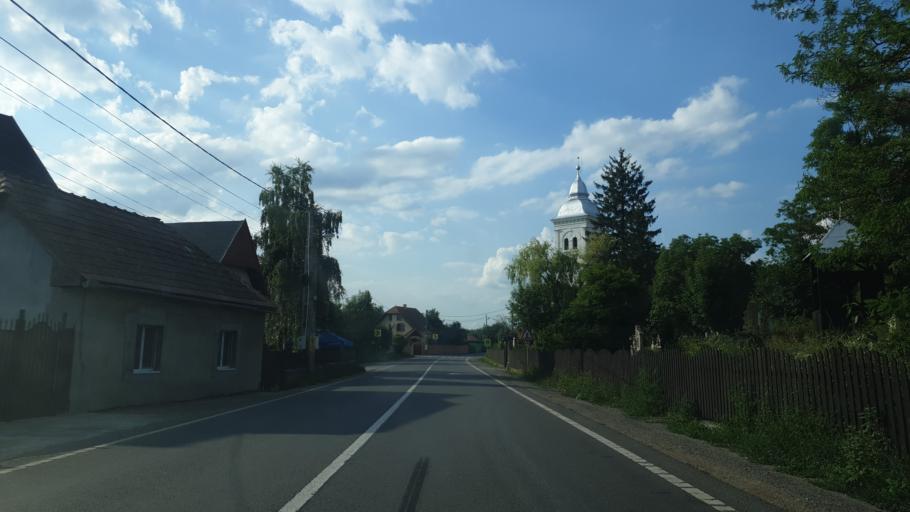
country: RO
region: Covasna
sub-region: Comuna Chichis
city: Chichis
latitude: 45.8122
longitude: 25.8000
